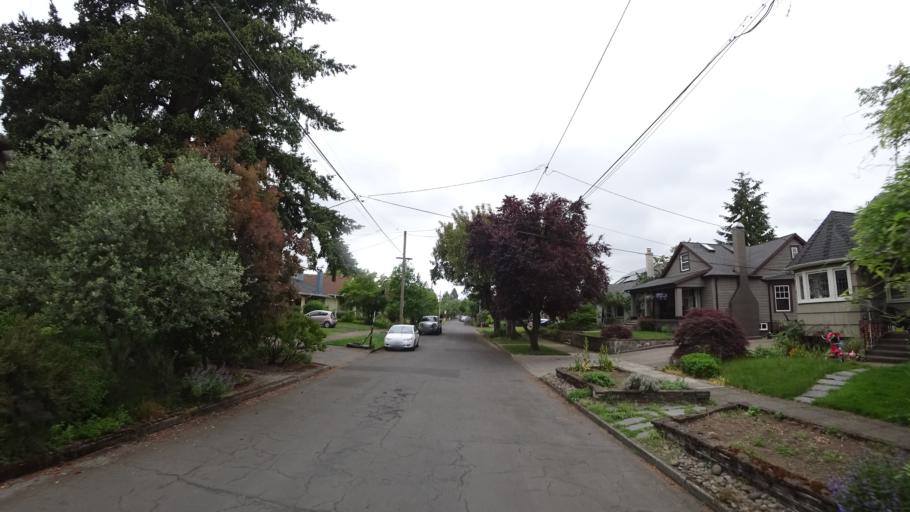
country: US
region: Oregon
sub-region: Multnomah County
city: Portland
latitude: 45.5430
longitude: -122.6107
